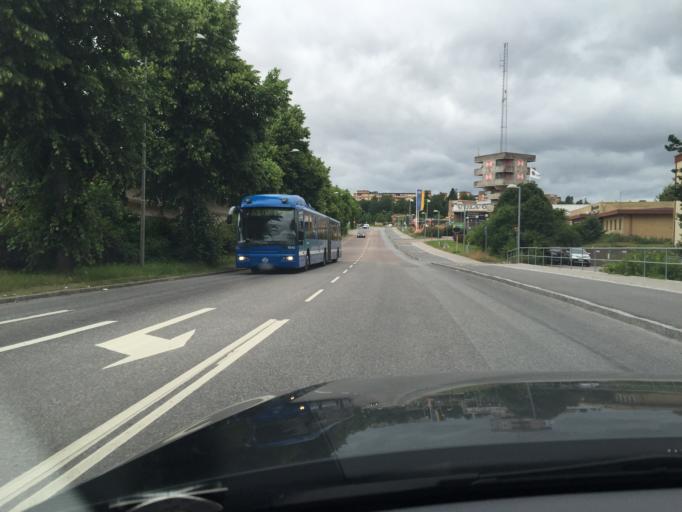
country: SE
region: Stockholm
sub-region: Stockholms Kommun
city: Kista
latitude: 59.4050
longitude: 17.9406
